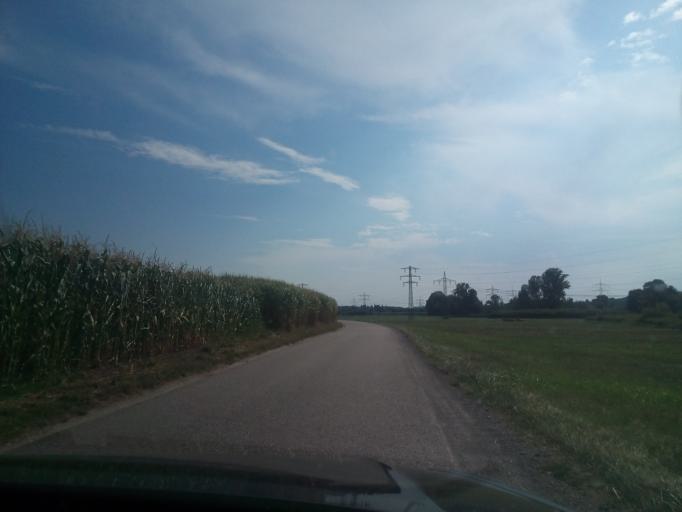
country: DE
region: Baden-Wuerttemberg
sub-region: Karlsruhe Region
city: Sinzheim
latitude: 48.7719
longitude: 8.1530
